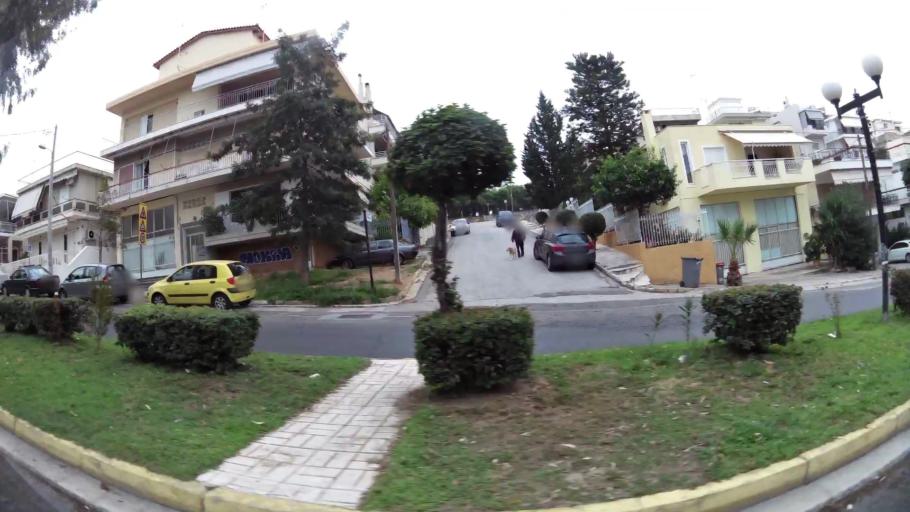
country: GR
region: Attica
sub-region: Nomarchia Athinas
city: Alimos
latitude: 37.9152
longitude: 23.7322
